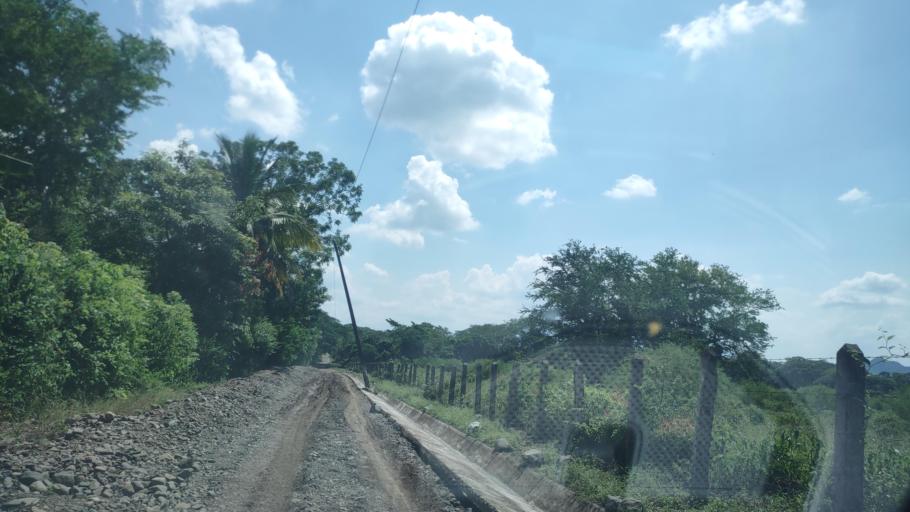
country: MX
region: Veracruz
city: Los Altos
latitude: 21.4309
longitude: -97.7916
